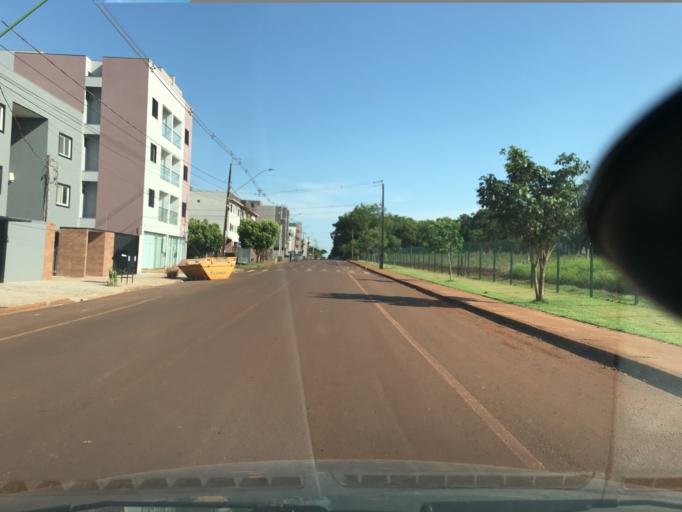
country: BR
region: Parana
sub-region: Palotina
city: Palotina
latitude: -24.2979
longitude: -53.8426
